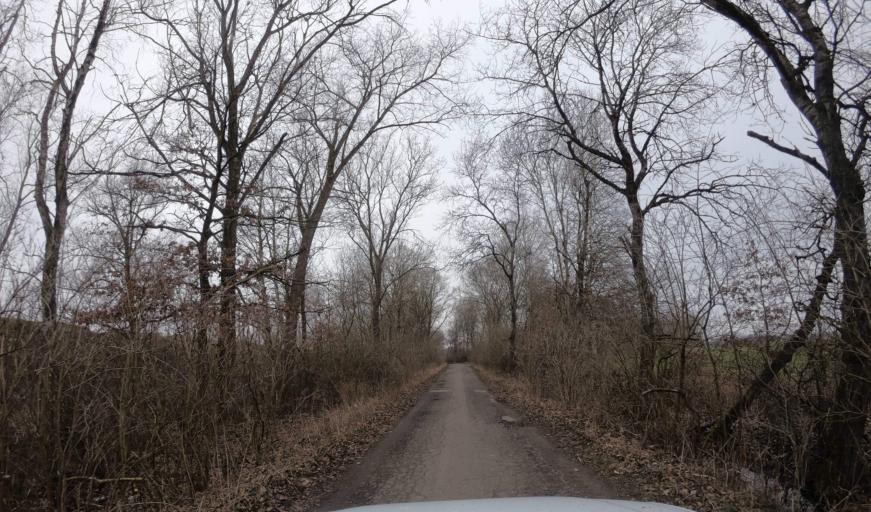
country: PL
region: West Pomeranian Voivodeship
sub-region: Powiat gryficki
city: Ploty
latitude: 53.8597
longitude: 15.2613
